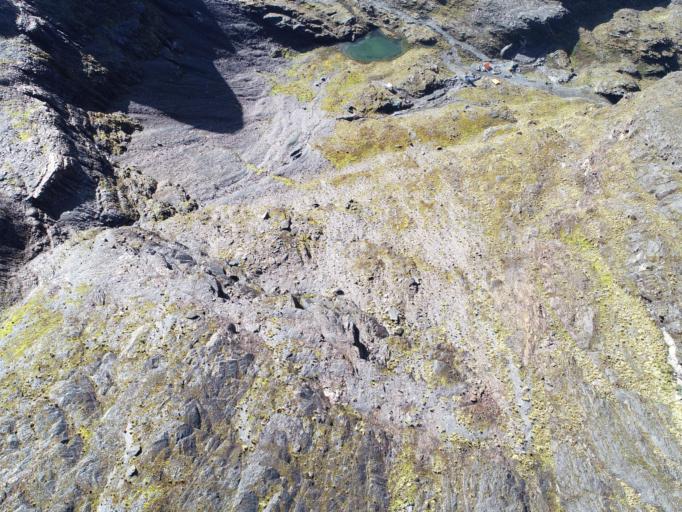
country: PE
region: Puno
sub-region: San Antonio De Putina
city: Sina
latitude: -14.7384
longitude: -69.0544
